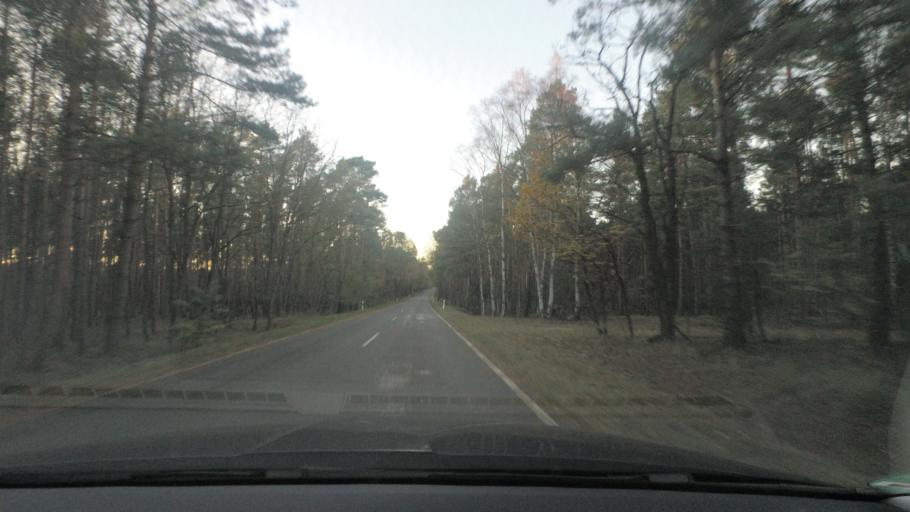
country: DE
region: Brandenburg
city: Ihlow
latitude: 51.9747
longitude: 13.3064
